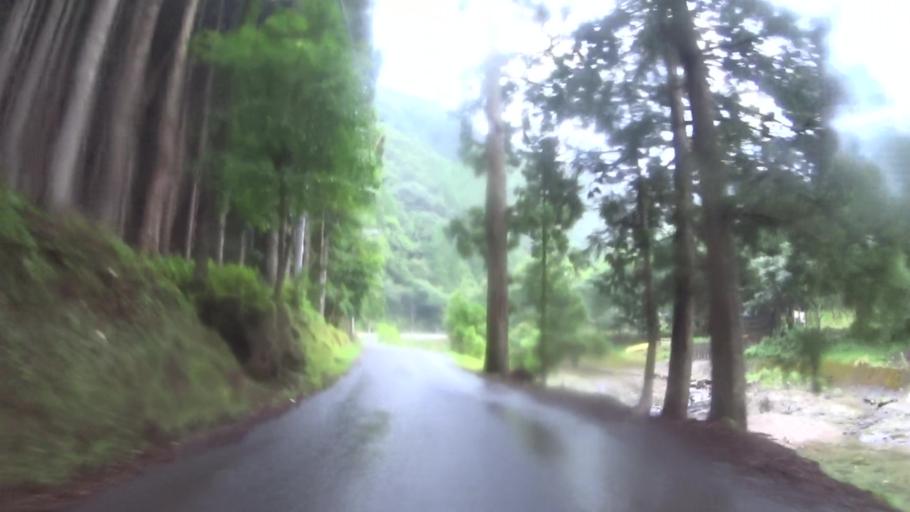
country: JP
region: Shiga Prefecture
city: Kitahama
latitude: 35.2790
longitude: 135.8474
